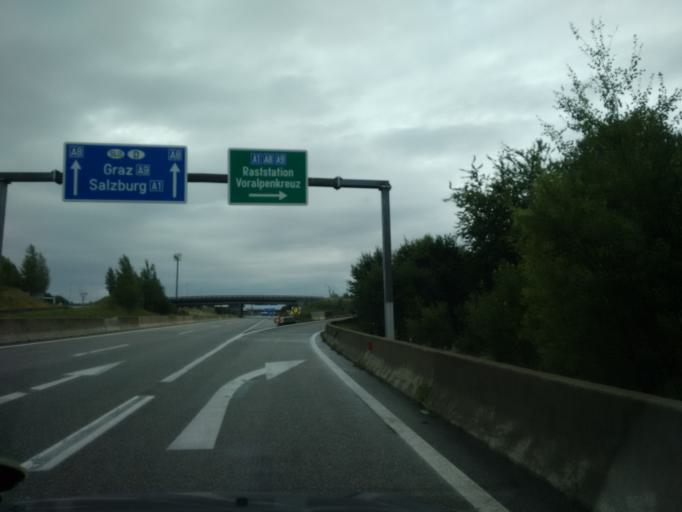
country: AT
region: Upper Austria
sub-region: Wels-Land
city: Sattledt
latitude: 48.0690
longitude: 14.0288
